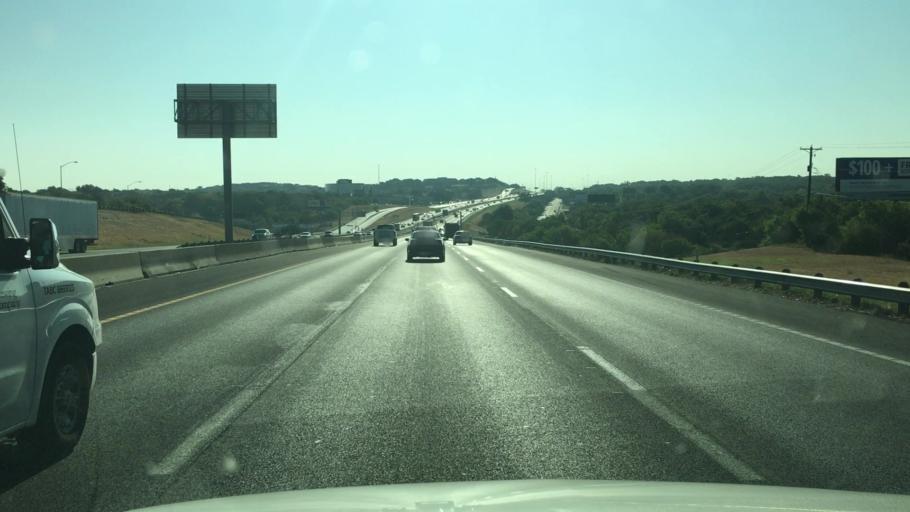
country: US
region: Texas
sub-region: Tarrant County
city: Haltom City
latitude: 32.7599
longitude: -97.2449
